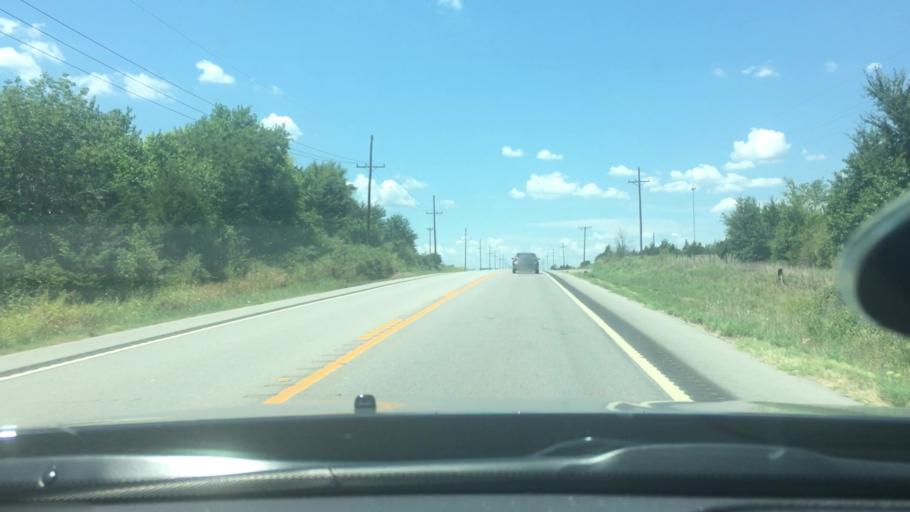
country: US
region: Oklahoma
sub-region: Bryan County
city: Durant
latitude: 33.9975
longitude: -96.2610
